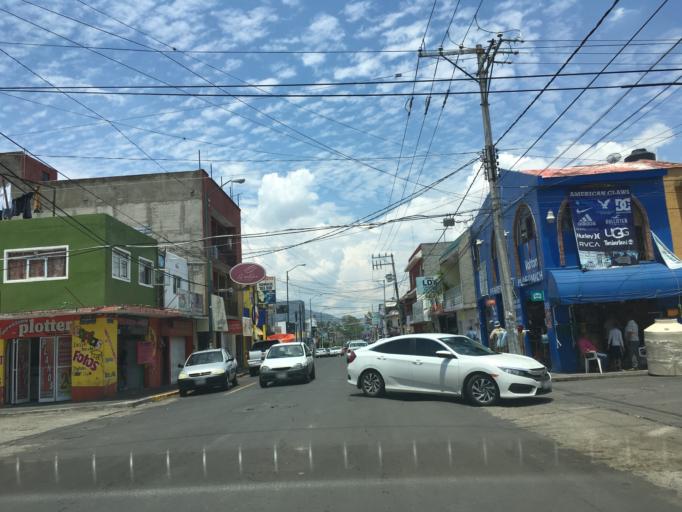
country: MX
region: Michoacan
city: Morelia
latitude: 19.6902
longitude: -101.1999
